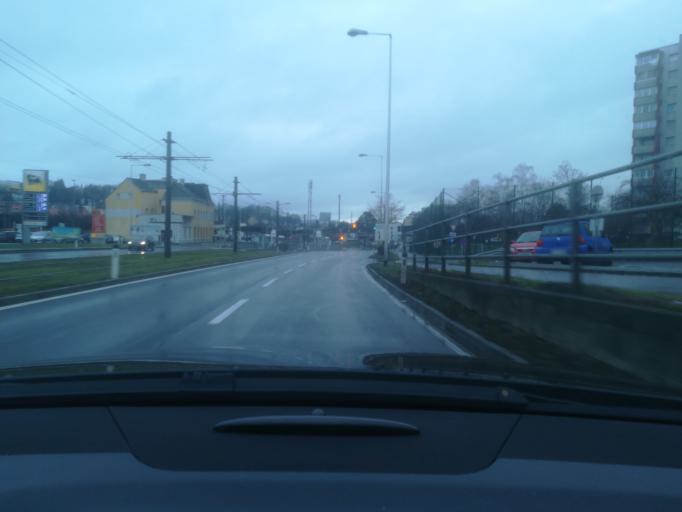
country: AT
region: Upper Austria
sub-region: Politischer Bezirk Linz-Land
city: Leonding
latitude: 48.2743
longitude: 14.2728
